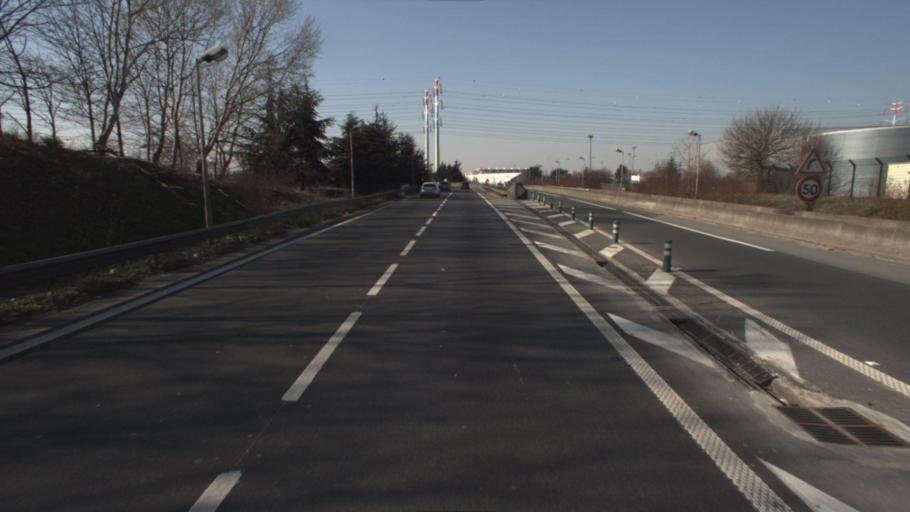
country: FR
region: Ile-de-France
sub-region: Departement du Val-de-Marne
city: Chevilly-Larue
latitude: 48.7575
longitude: 2.3402
